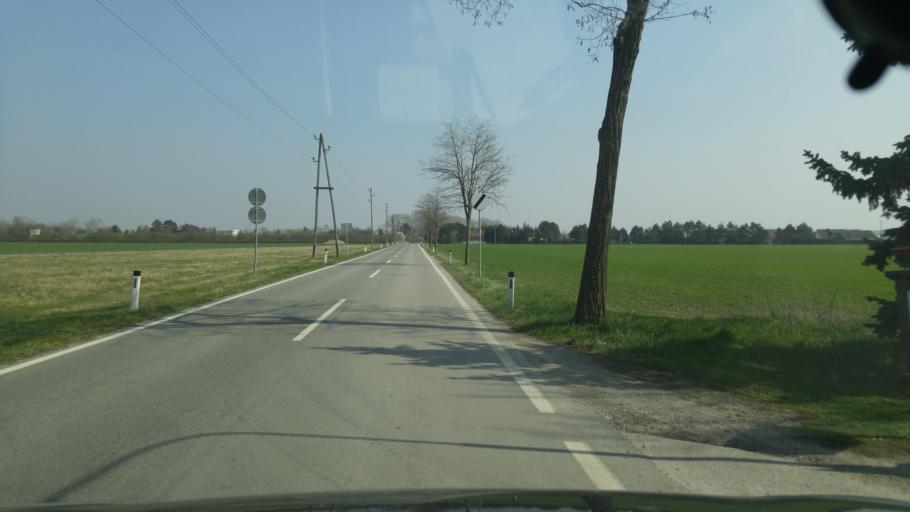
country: AT
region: Lower Austria
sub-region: Politischer Bezirk Modling
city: Munchendorf
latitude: 48.0337
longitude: 16.4051
